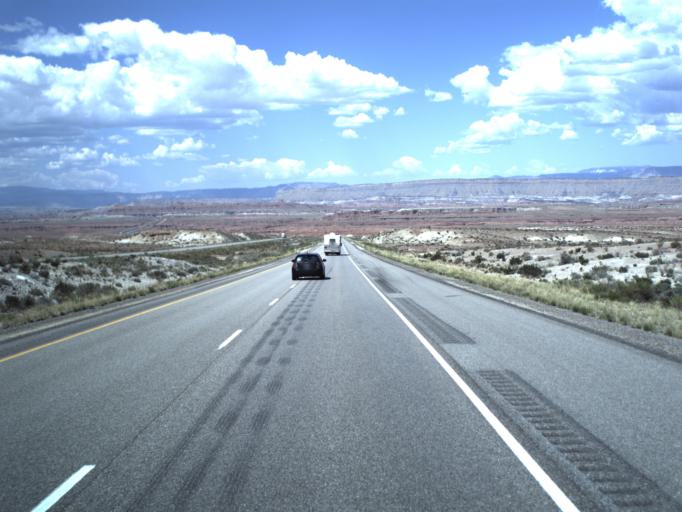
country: US
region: Utah
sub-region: Emery County
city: Ferron
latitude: 38.8468
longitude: -110.9973
